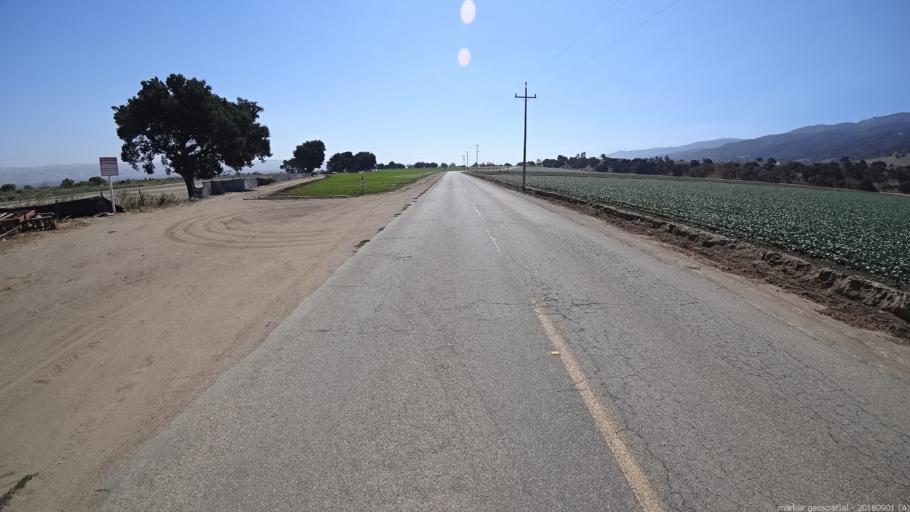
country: US
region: California
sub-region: Monterey County
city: Chualar
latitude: 36.5289
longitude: -121.5291
